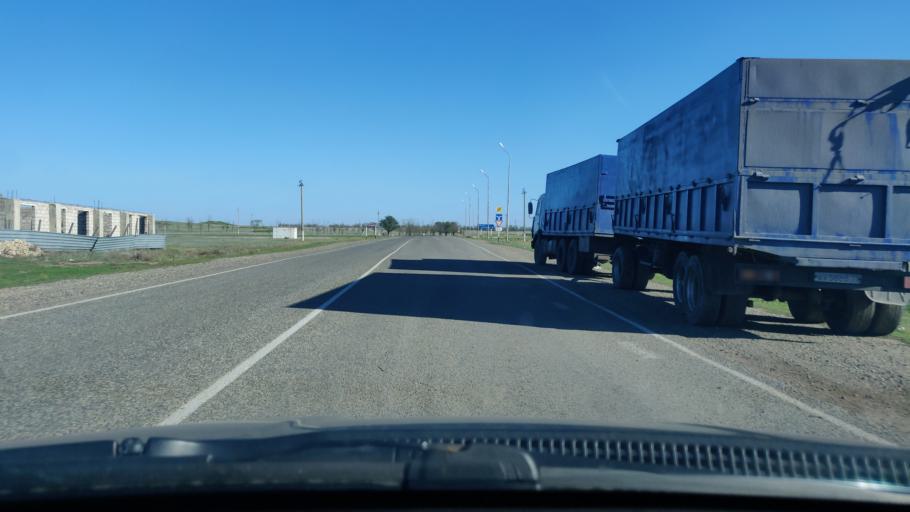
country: RU
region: Stavropol'skiy
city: Letnyaya Stavka
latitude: 45.3733
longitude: 43.6904
